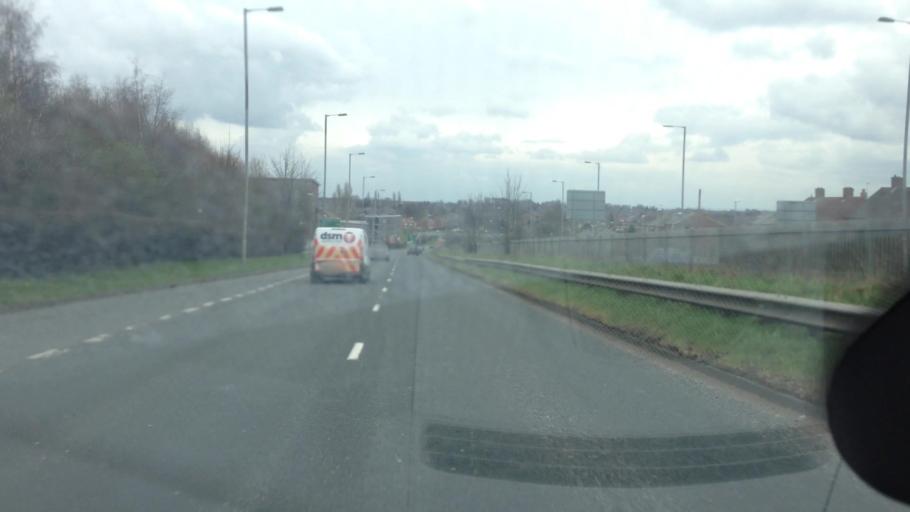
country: GB
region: England
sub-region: City and Borough of Leeds
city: Scholes
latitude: 53.8209
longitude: -1.4555
